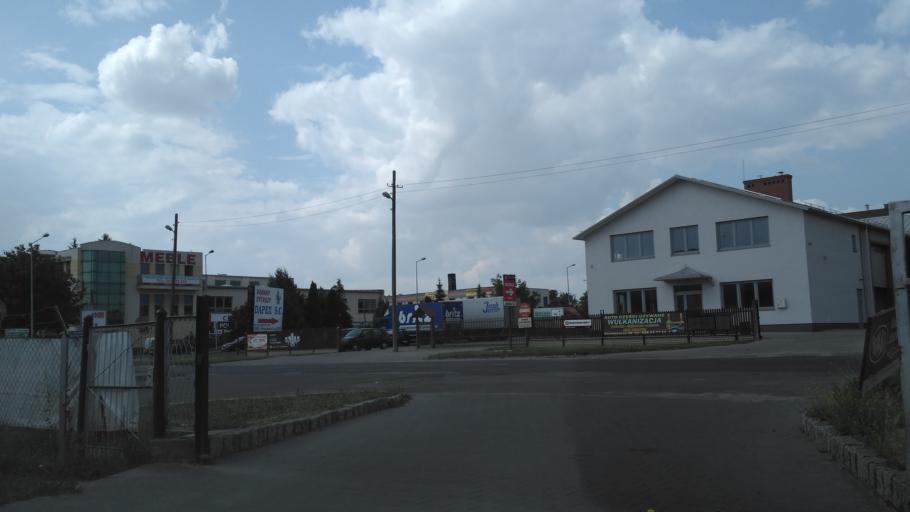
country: PL
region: Lublin Voivodeship
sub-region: Chelm
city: Chelm
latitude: 51.1423
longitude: 23.4944
